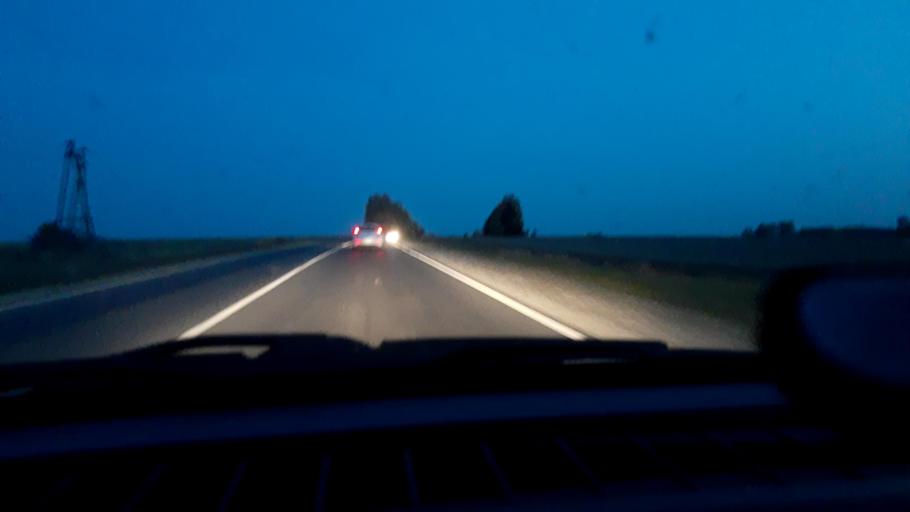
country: RU
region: Nizjnij Novgorod
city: Gorodets
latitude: 56.6284
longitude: 43.5422
